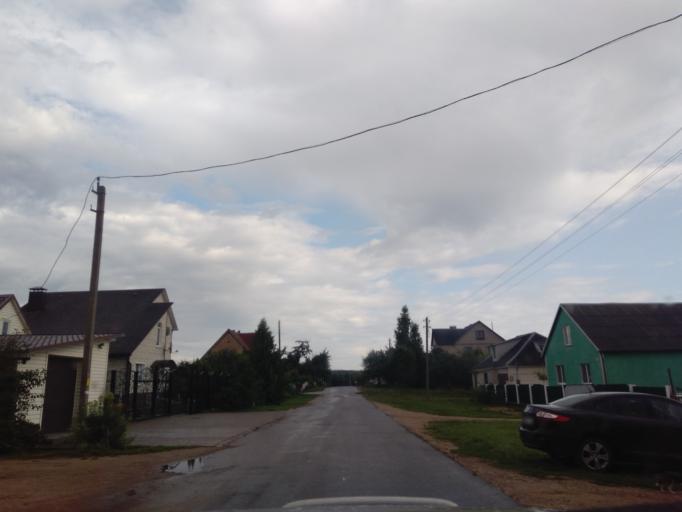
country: BY
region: Minsk
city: Kapyl'
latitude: 53.1658
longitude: 27.0885
